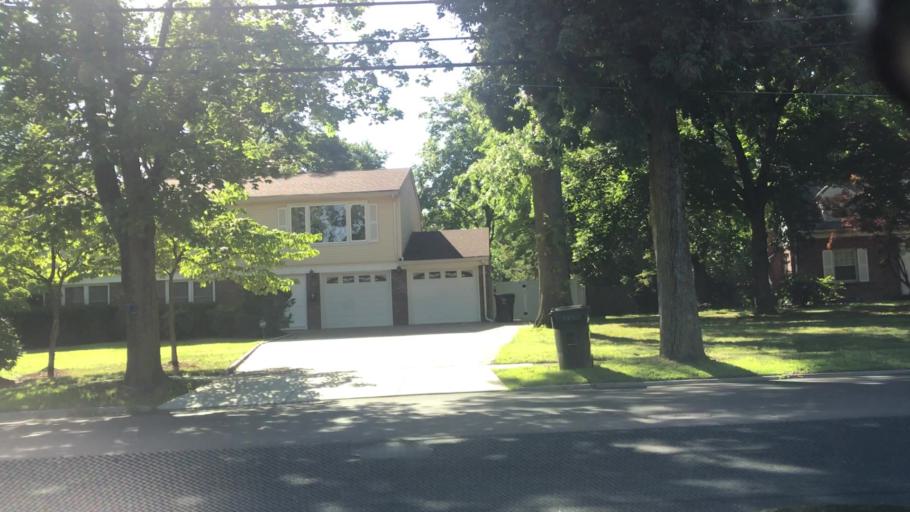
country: US
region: New Jersey
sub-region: Bergen County
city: Maywood
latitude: 40.9209
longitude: -74.0605
